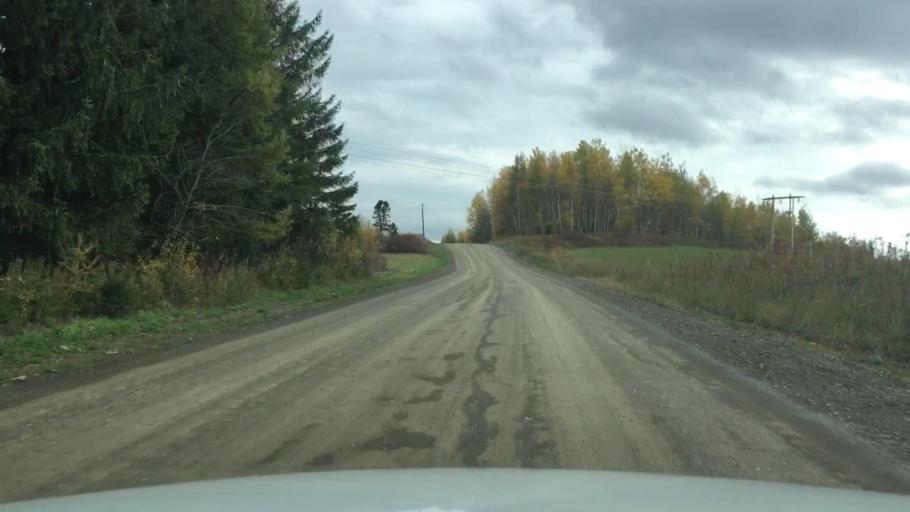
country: US
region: Maine
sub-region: Aroostook County
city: Easton
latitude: 46.5178
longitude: -67.8852
